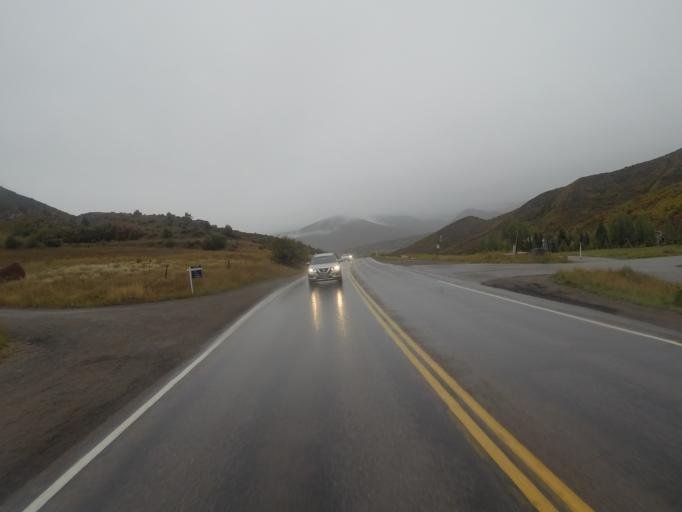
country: US
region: Colorado
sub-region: Pitkin County
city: Snowmass Village
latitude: 39.2394
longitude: -106.8966
